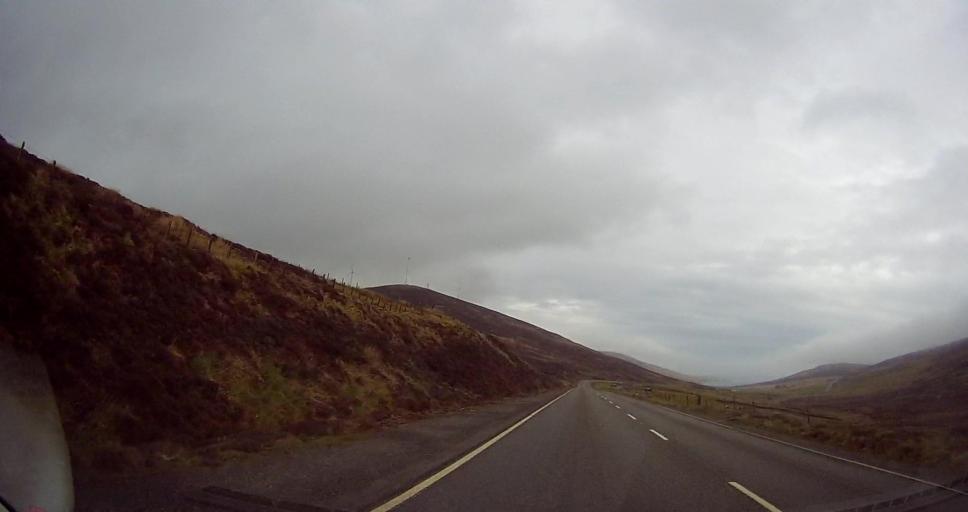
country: GB
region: Scotland
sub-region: Shetland Islands
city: Lerwick
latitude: 60.1525
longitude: -1.2363
